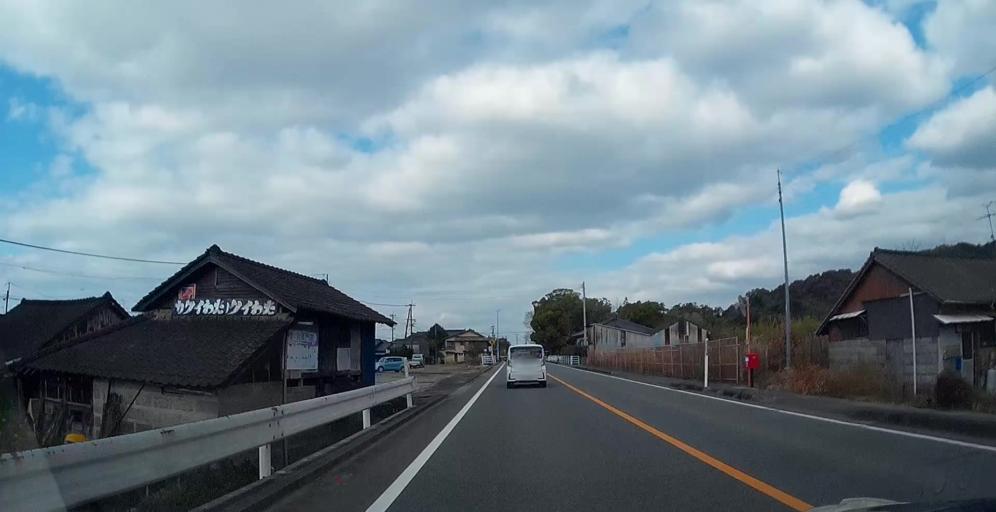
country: JP
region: Kumamoto
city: Yatsushiro
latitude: 32.4438
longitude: 130.5864
